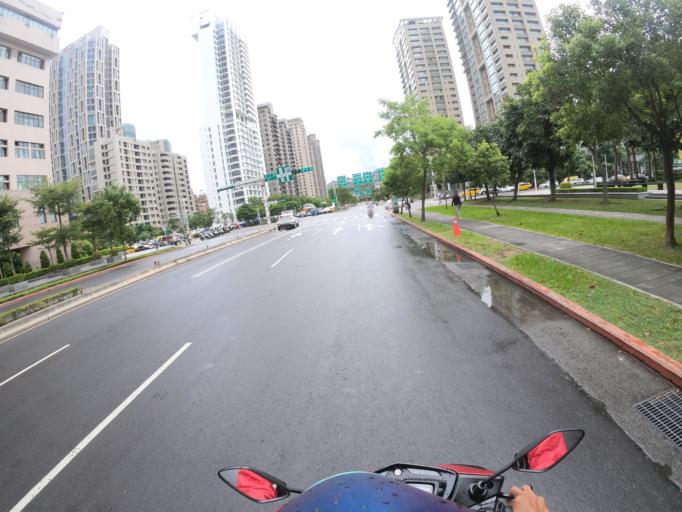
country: TW
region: Taipei
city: Taipei
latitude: 25.0324
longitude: 121.5671
